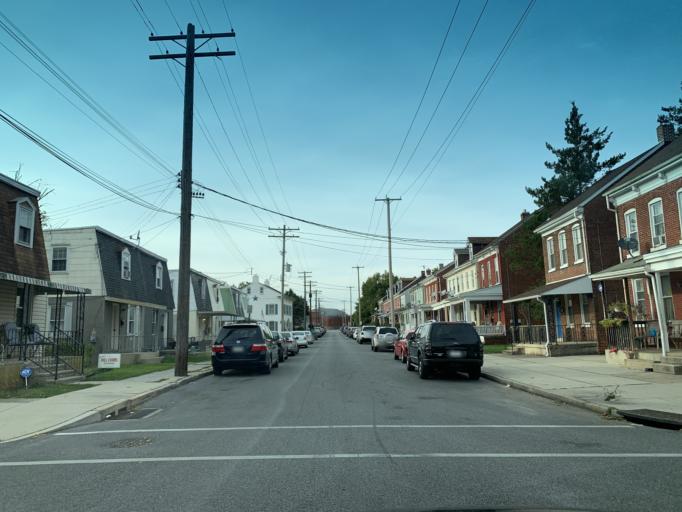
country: US
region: Pennsylvania
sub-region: York County
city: North York
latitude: 39.9688
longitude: -76.7378
